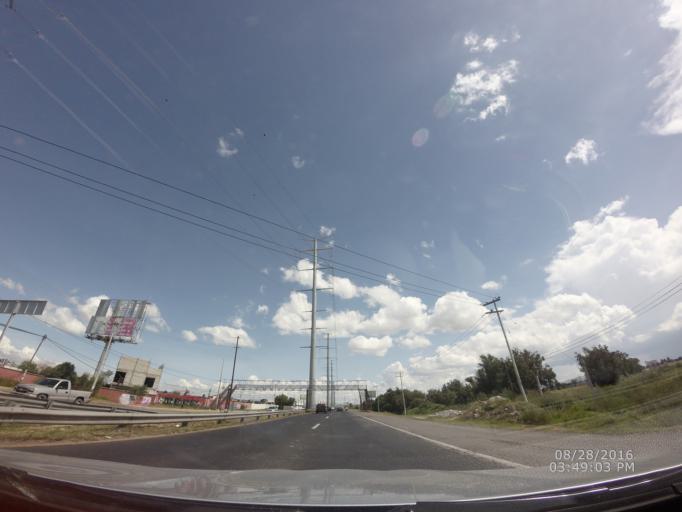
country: MX
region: Hidalgo
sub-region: Mineral de la Reforma
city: Los Tuzos
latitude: 20.0482
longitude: -98.7376
